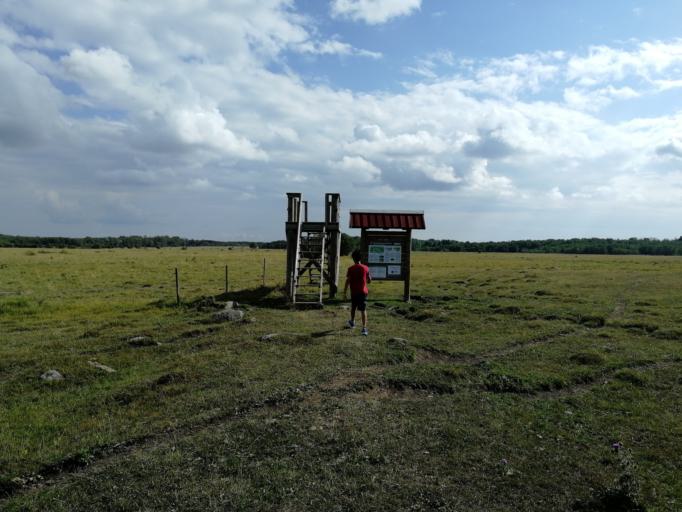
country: EE
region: Laeaene
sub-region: Lihula vald
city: Lihula
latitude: 58.7237
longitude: 23.7925
